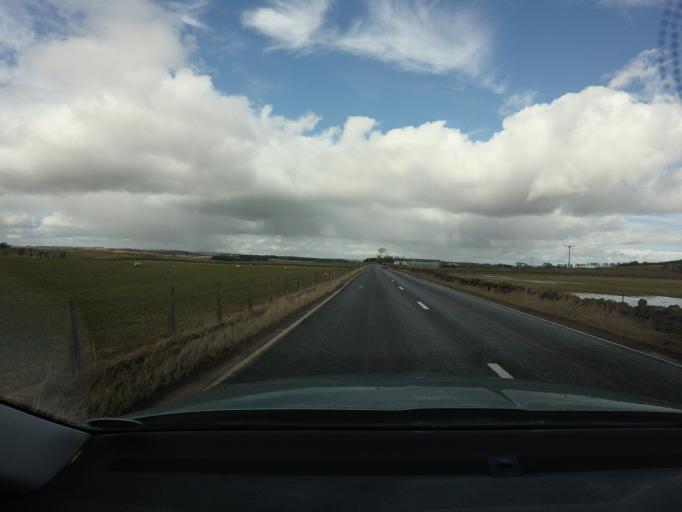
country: GB
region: Scotland
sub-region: South Lanarkshire
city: Lanark
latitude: 55.6327
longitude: -3.7441
